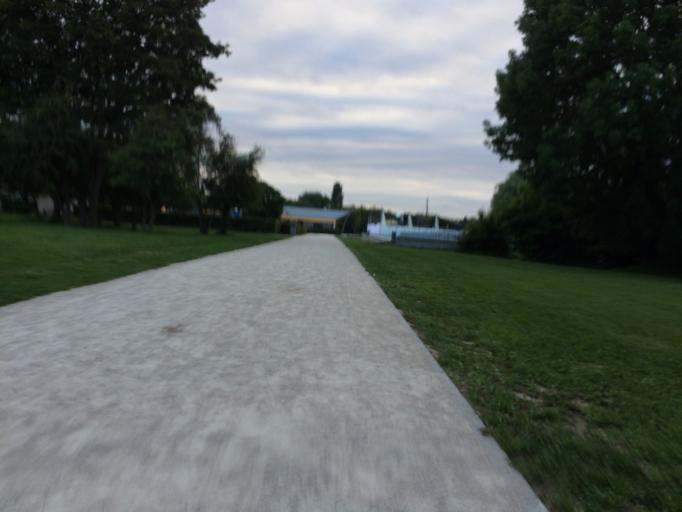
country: FR
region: Ile-de-France
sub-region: Departement de l'Essonne
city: Juvisy-sur-Orge
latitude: 48.6899
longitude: 2.3938
